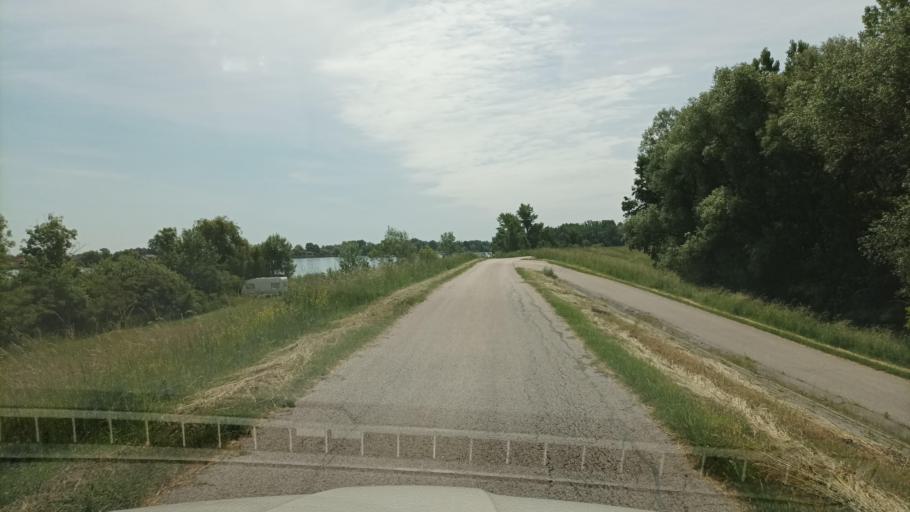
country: HU
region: Fejer
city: Racalmas
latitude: 47.0445
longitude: 18.9714
